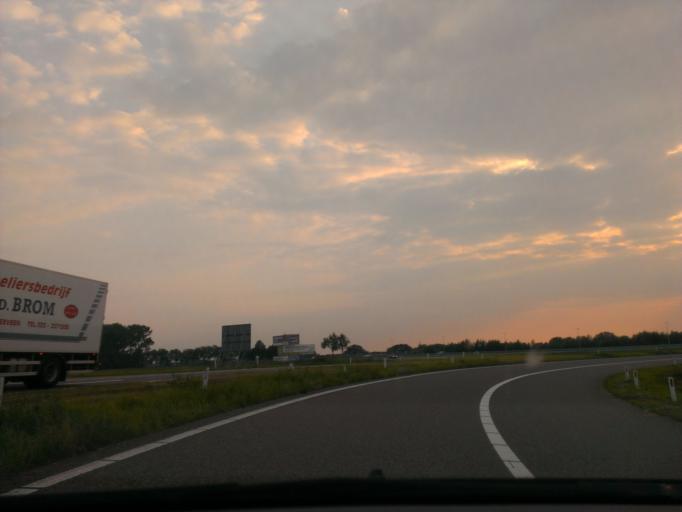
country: NL
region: Gelderland
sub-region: Gemeente Nijkerk
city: Nijkerk
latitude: 52.2087
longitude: 5.4446
